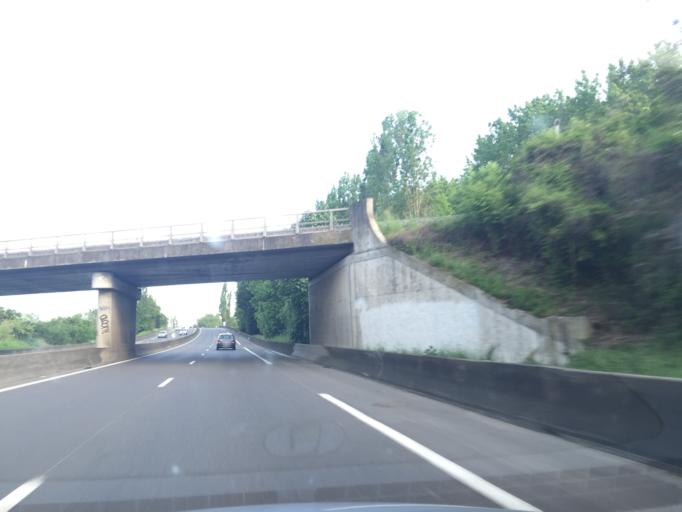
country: FR
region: Auvergne
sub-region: Departement du Puy-de-Dome
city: Riom
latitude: 45.9005
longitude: 3.1340
